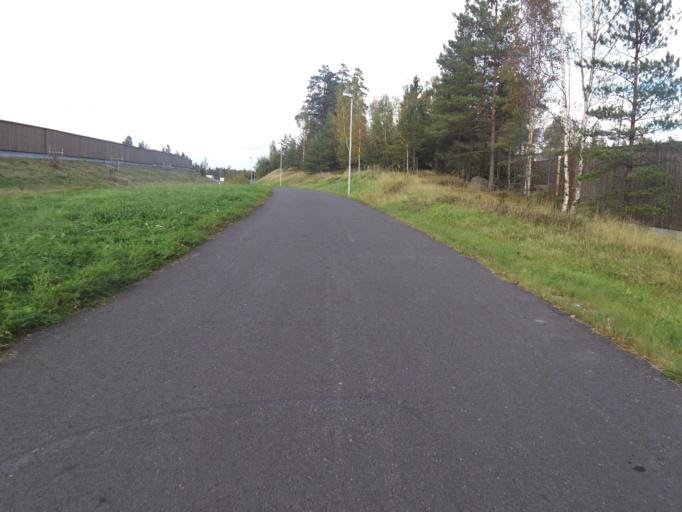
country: FI
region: Uusimaa
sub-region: Helsinki
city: Kauniainen
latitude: 60.2308
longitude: 24.6880
